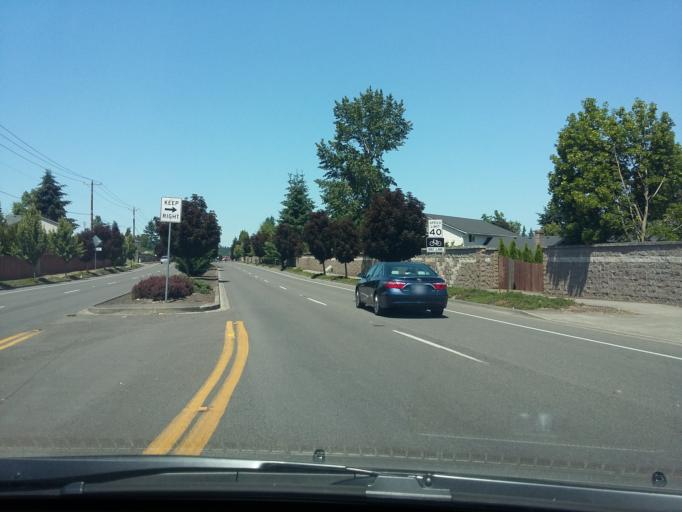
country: US
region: Washington
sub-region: Clark County
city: Orchards
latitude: 45.6716
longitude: -122.5679
